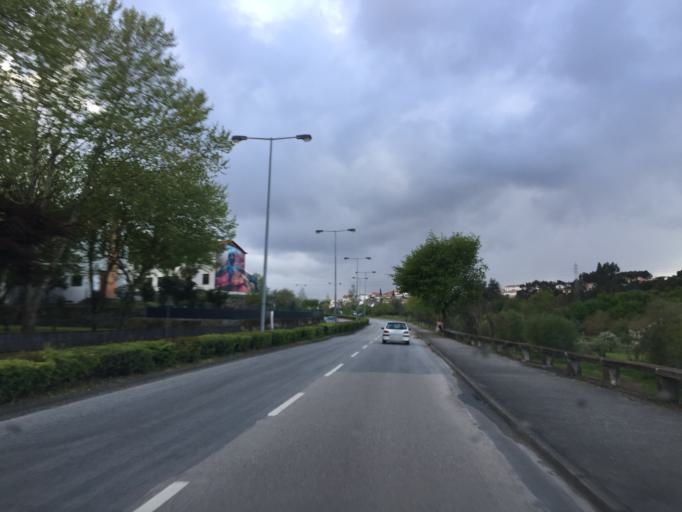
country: PT
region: Viseu
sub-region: Viseu
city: Viseu
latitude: 40.6628
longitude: -7.9208
